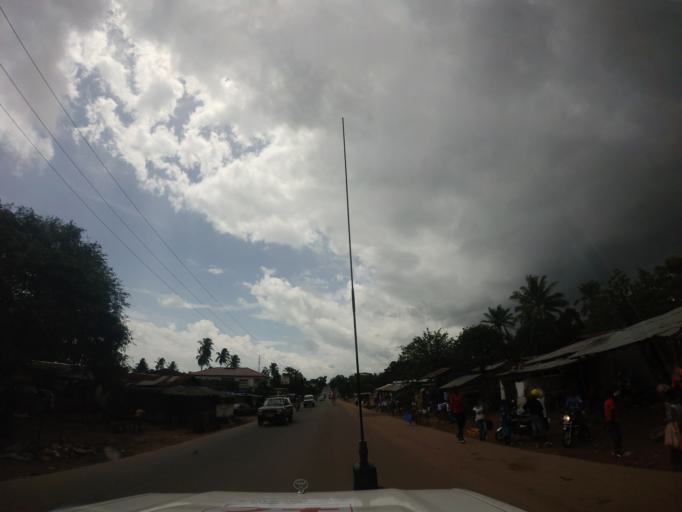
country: SL
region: Western Area
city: Waterloo
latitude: 8.3267
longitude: -13.0621
